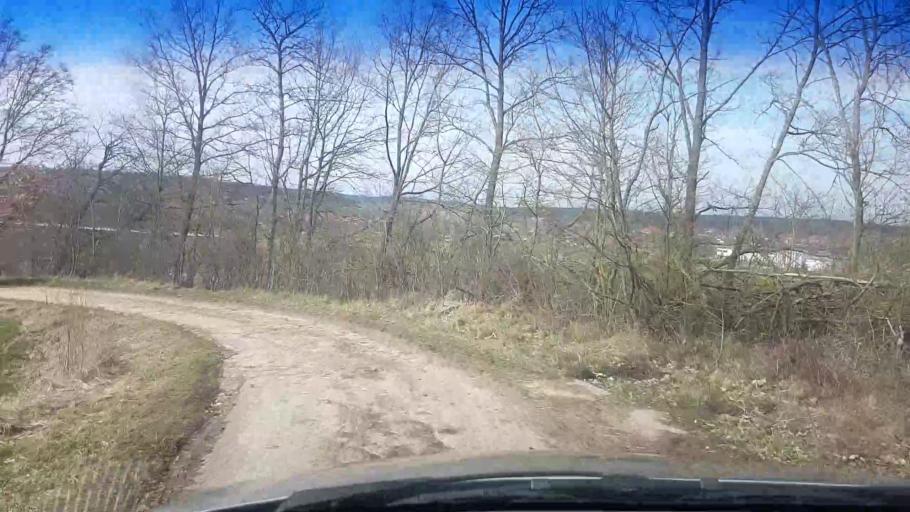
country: DE
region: Bavaria
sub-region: Upper Franconia
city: Burgebrach
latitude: 49.8228
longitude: 10.7557
